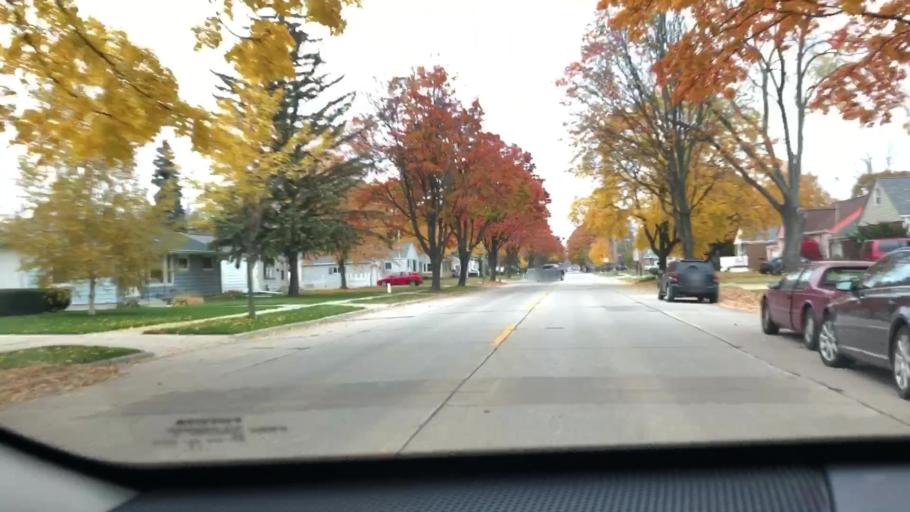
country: US
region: Wisconsin
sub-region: Brown County
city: Green Bay
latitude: 44.5123
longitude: -88.0496
